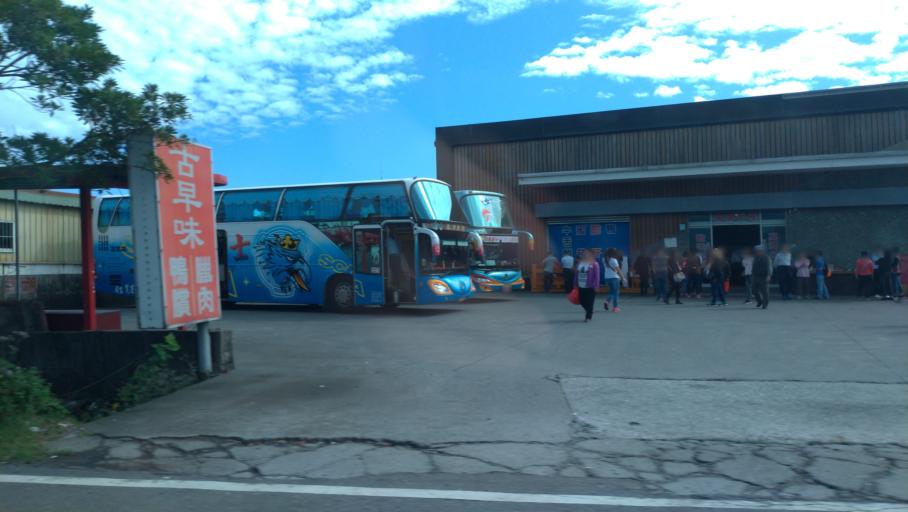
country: TW
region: Taiwan
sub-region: Yilan
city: Yilan
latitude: 24.7810
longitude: 121.7834
